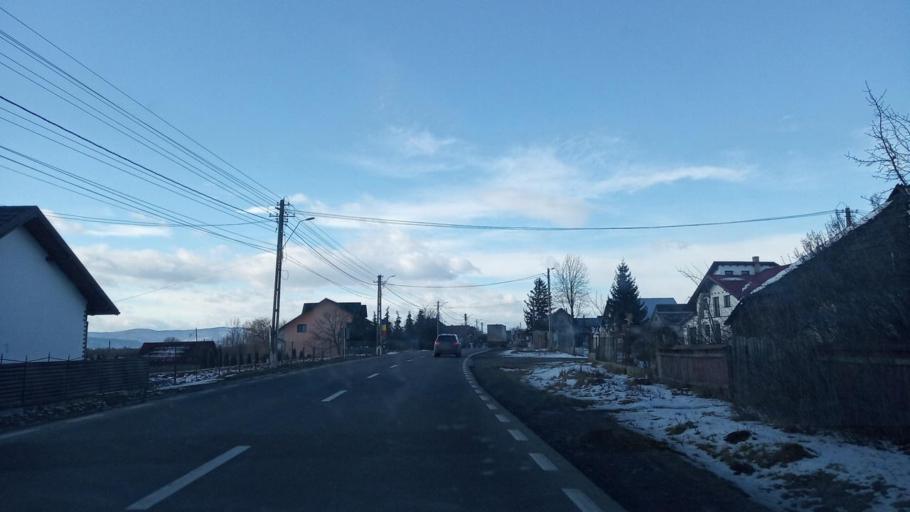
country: RO
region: Suceava
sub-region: Comuna Cornu Luncii
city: Baisesti
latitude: 47.4857
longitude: 26.0917
